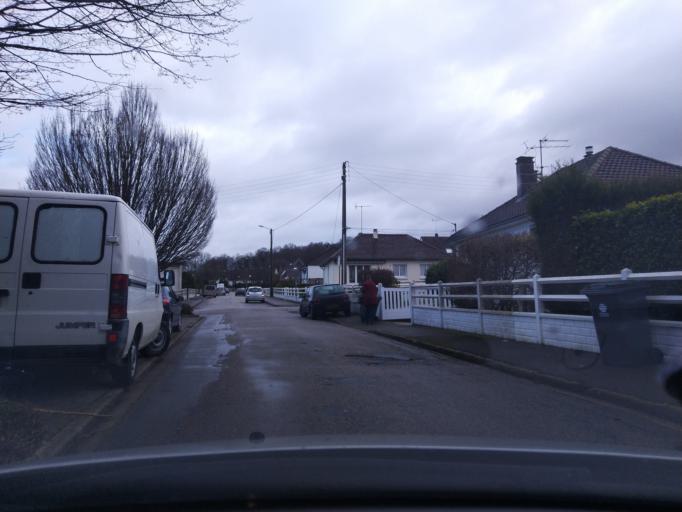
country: FR
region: Haute-Normandie
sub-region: Departement de la Seine-Maritime
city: Duclair
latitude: 49.4891
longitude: 0.8818
